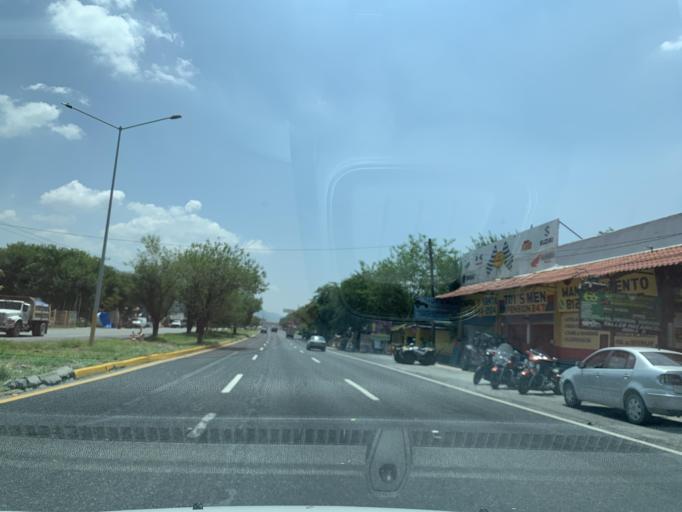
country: MX
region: Nuevo Leon
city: Santiago
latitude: 25.4592
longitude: -100.1691
